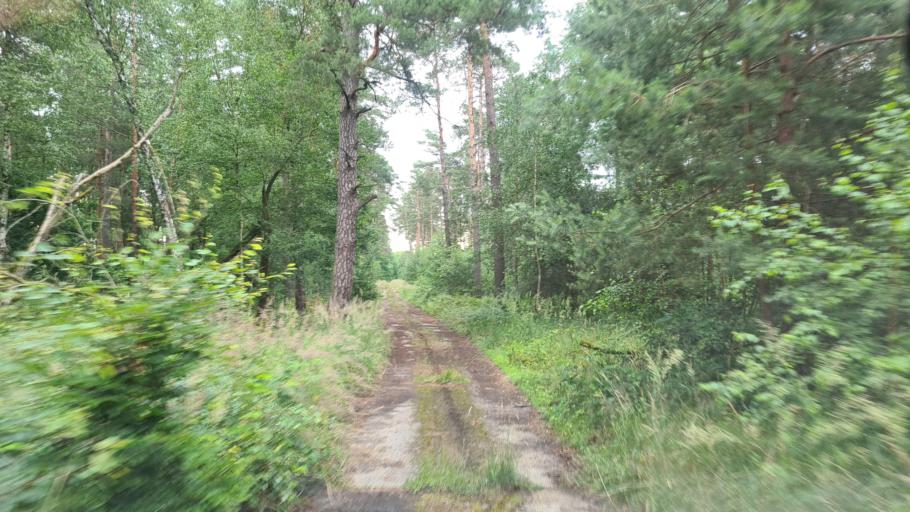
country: DE
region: Brandenburg
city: Crinitz
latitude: 51.7189
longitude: 13.7307
